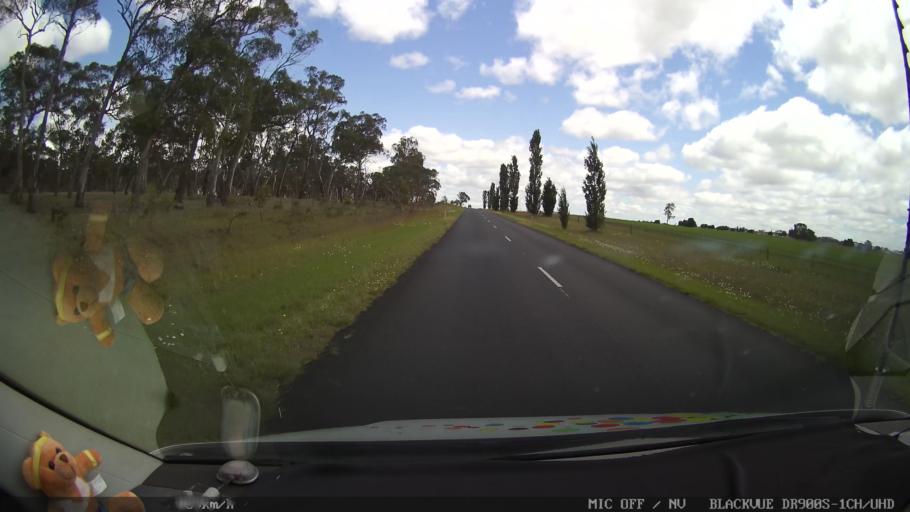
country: AU
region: New South Wales
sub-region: Glen Innes Severn
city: Glen Innes
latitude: -29.6646
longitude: 151.6935
